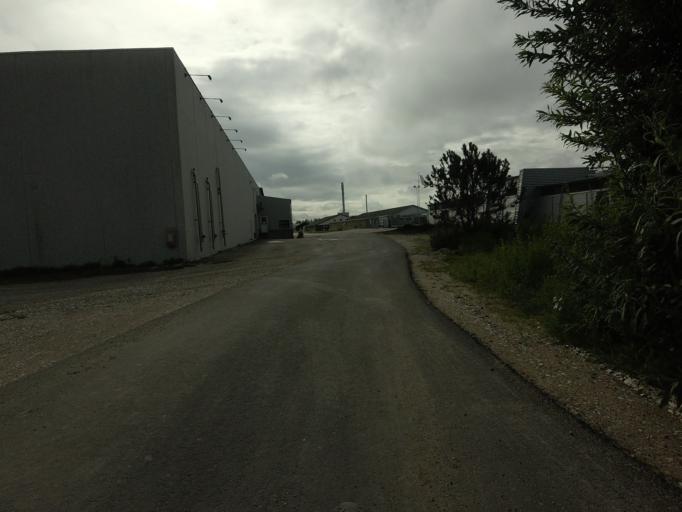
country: DK
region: North Denmark
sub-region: Jammerbugt Kommune
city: Pandrup
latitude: 57.3710
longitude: 9.7339
